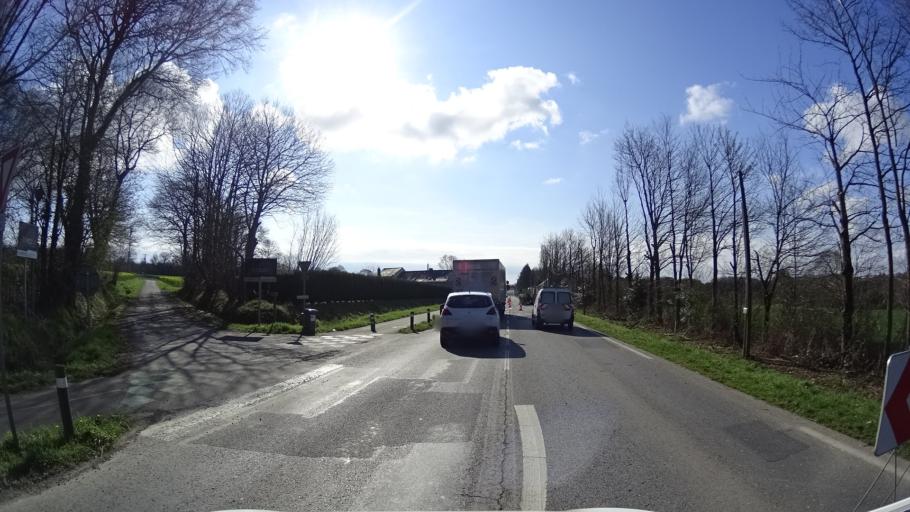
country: FR
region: Brittany
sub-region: Departement d'Ille-et-Vilaine
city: La Meziere
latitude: 48.2113
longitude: -1.7427
